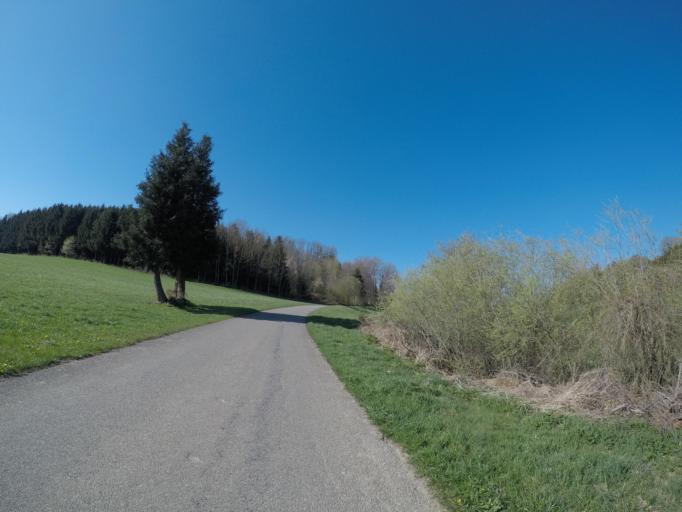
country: DE
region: Baden-Wuerttemberg
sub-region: Tuebingen Region
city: Ebenweiler
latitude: 47.8784
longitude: 9.5125
